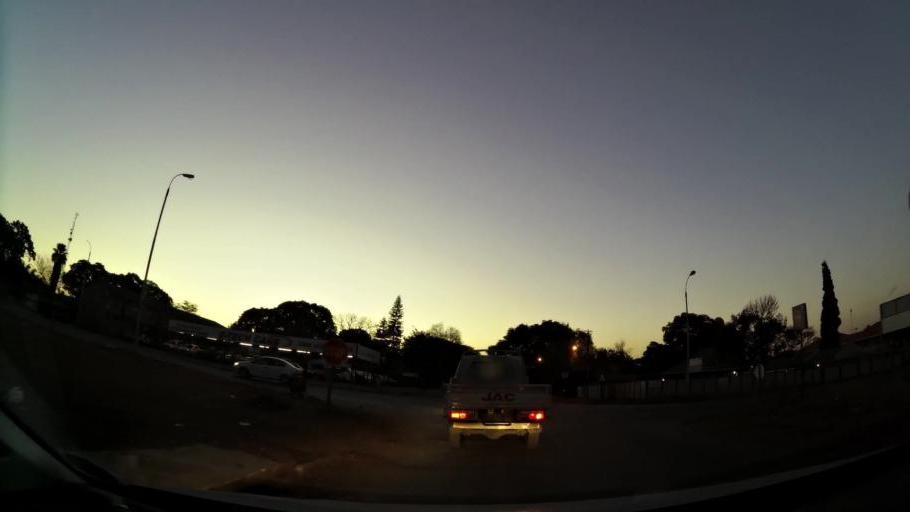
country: ZA
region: North-West
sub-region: Bojanala Platinum District Municipality
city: Rustenburg
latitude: -25.6728
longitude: 27.2522
